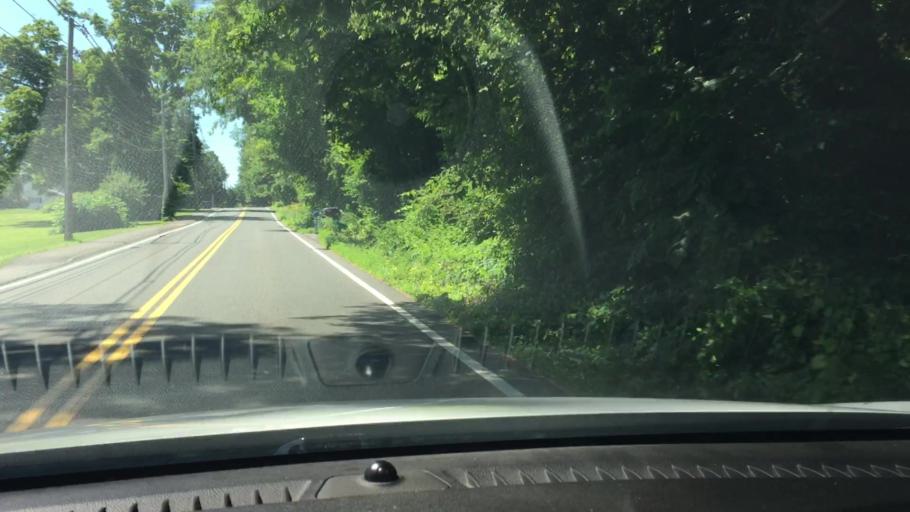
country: US
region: Massachusetts
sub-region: Berkshire County
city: Lenox
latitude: 42.3609
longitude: -73.2595
